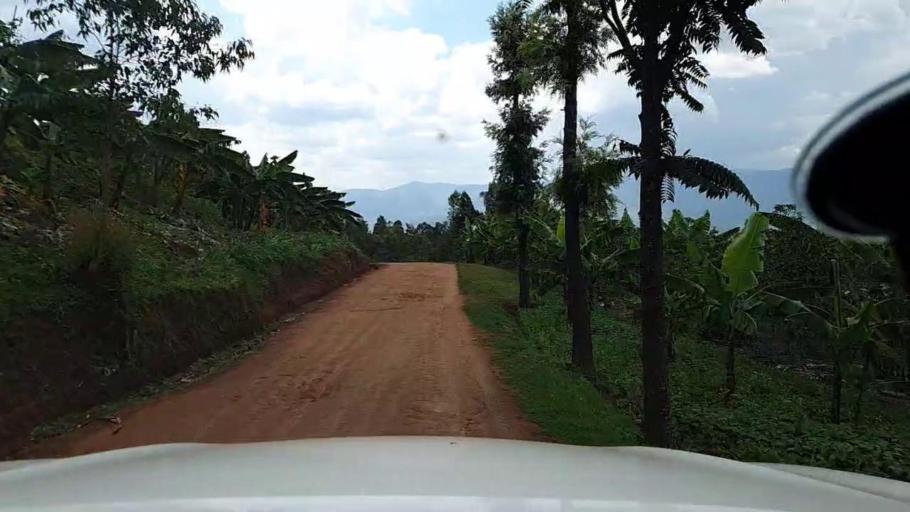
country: RW
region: Southern Province
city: Gitarama
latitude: -1.8387
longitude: 29.8277
